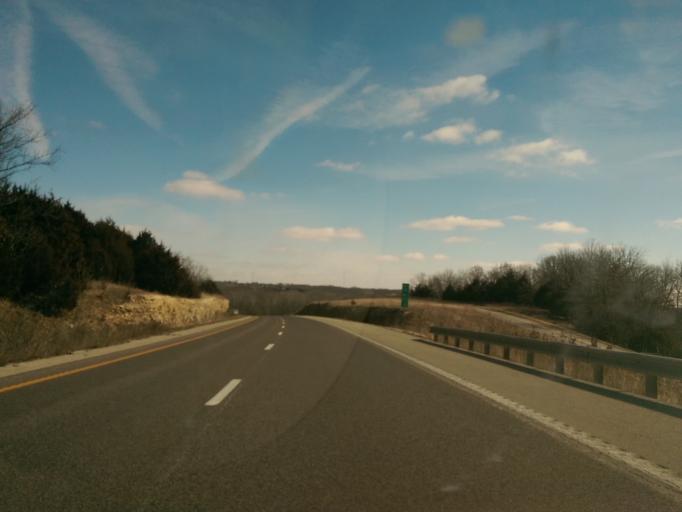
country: US
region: Missouri
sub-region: Callaway County
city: Fulton
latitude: 38.9358
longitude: -91.8514
